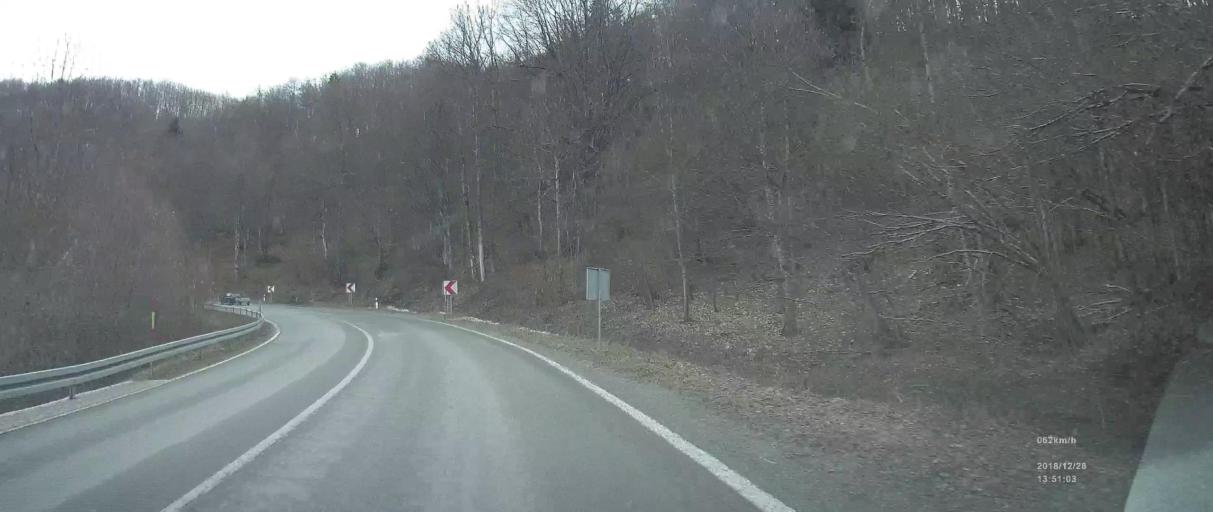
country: HR
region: Primorsko-Goranska
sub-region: Grad Delnice
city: Delnice
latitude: 45.3922
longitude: 14.8357
